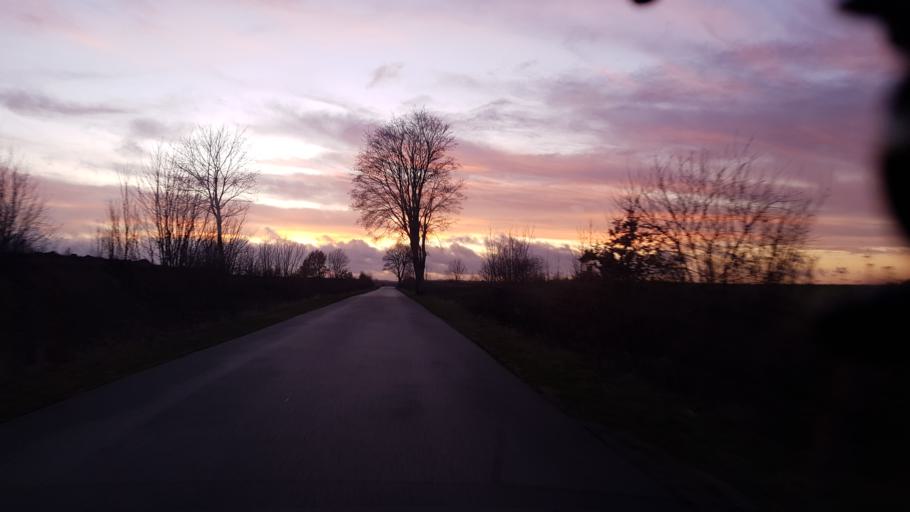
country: PL
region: Pomeranian Voivodeship
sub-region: Powiat bytowski
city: Tuchomie
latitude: 54.1302
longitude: 17.3548
